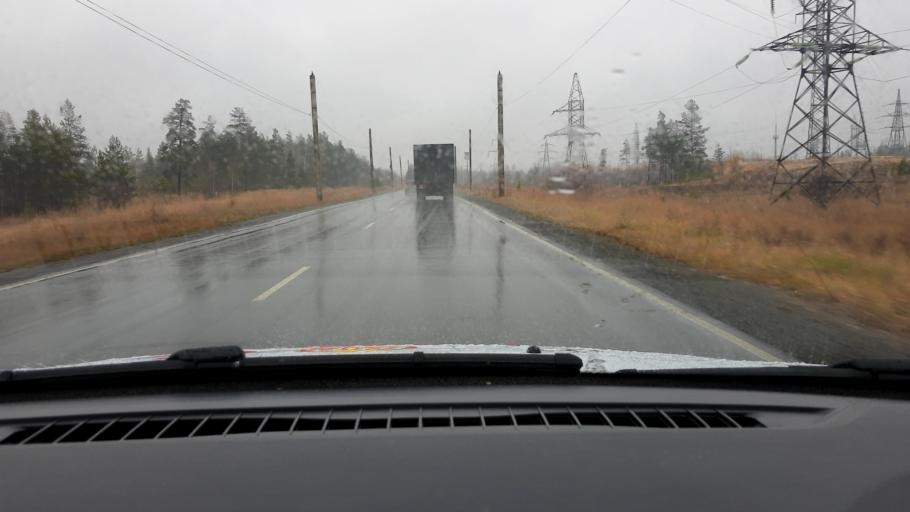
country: RU
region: Nizjnij Novgorod
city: Babino
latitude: 56.2842
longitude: 43.5796
